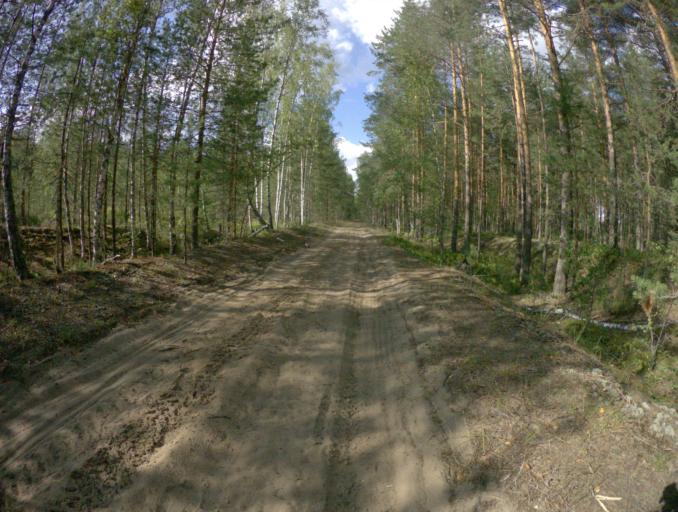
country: RU
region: Vladimir
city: Sobinka
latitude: 55.9481
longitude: 40.0589
